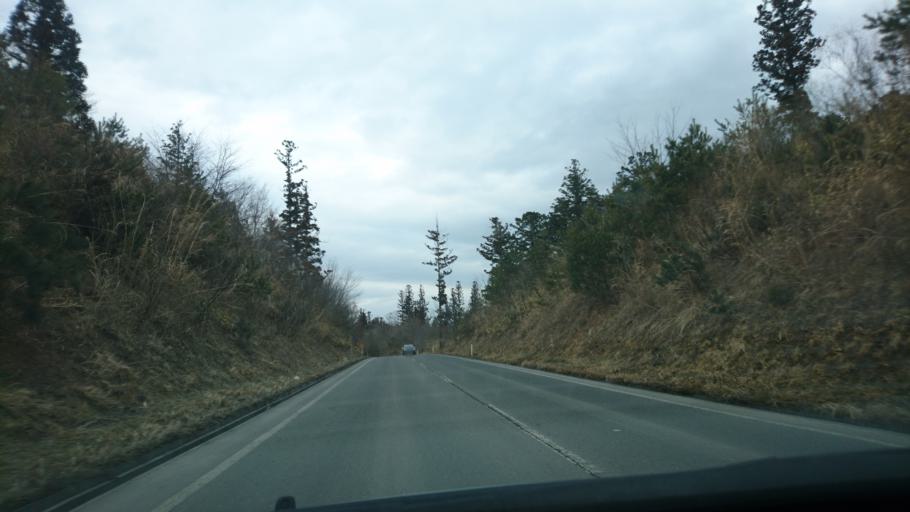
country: JP
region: Iwate
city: Ichinoseki
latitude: 38.9877
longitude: 141.3574
